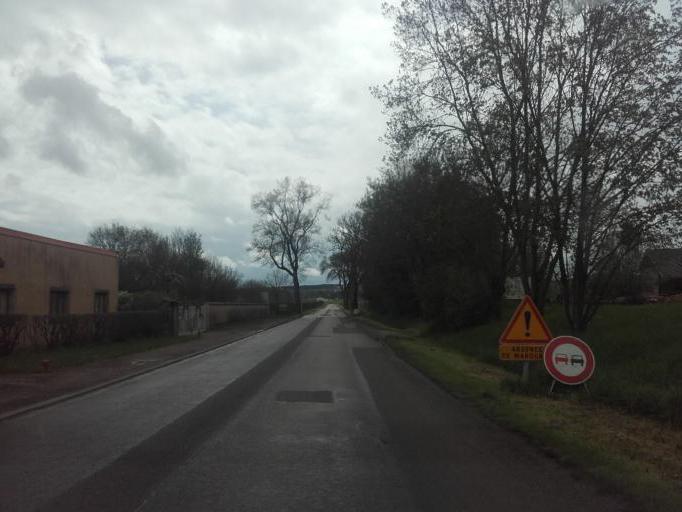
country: FR
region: Bourgogne
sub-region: Departement de l'Yonne
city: Chablis
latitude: 47.8081
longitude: 3.7990
